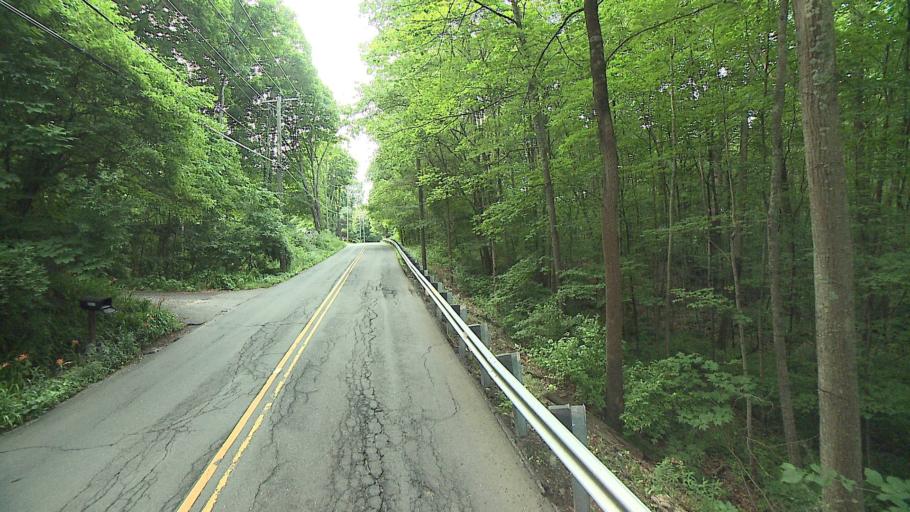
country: US
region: Connecticut
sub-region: New Haven County
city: Southbury
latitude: 41.4377
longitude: -73.1918
